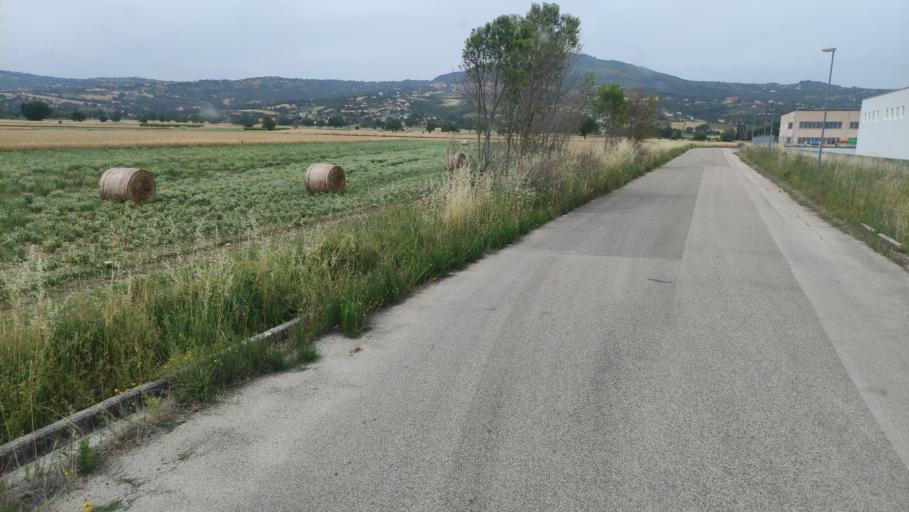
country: IT
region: Campania
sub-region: Provincia di Avellino
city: Sturno
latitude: 41.0465
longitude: 15.1304
